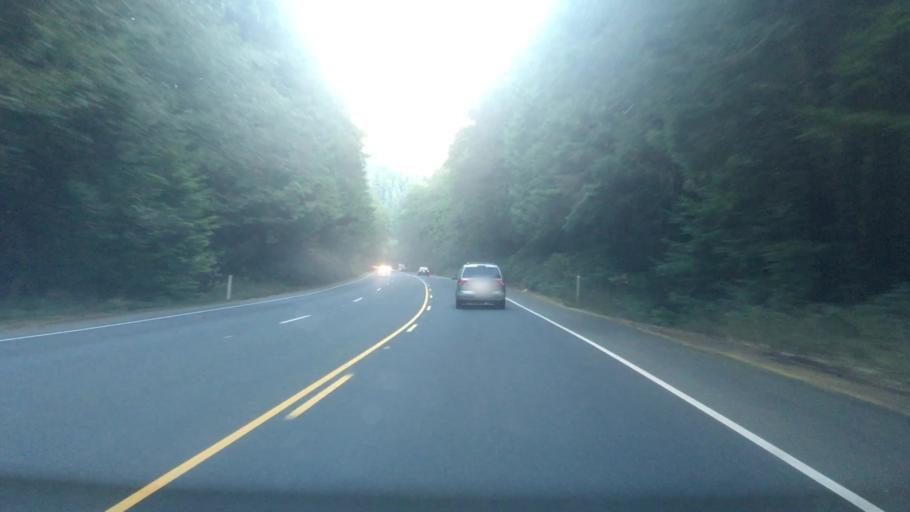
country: US
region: Oregon
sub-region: Clatsop County
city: Cannon Beach
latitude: 45.7785
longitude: -123.9521
